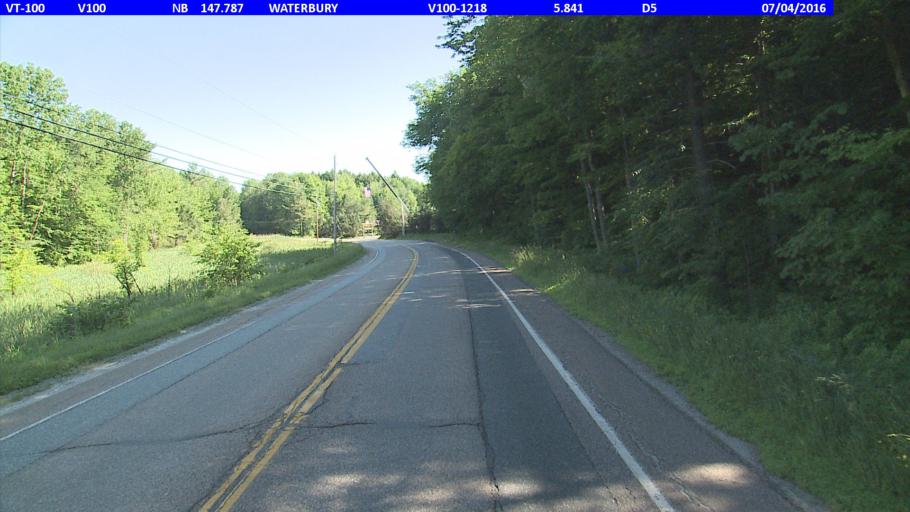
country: US
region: Vermont
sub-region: Washington County
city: Waterbury
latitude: 44.4128
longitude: -72.7215
